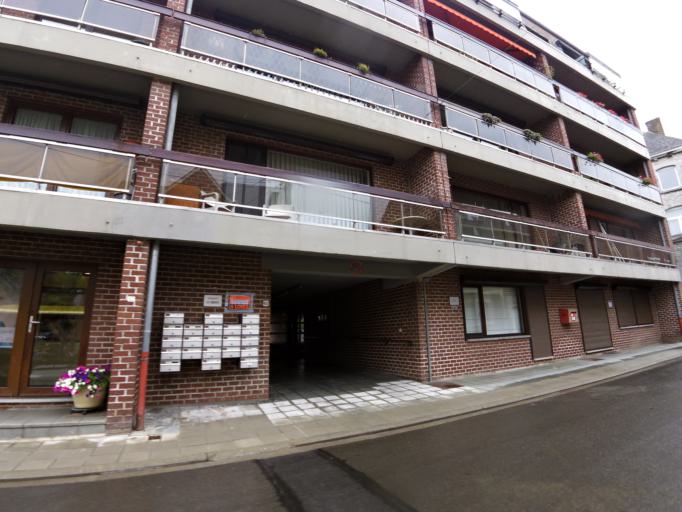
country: BE
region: Wallonia
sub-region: Province de Namur
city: Rochefort
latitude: 50.1601
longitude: 5.2188
